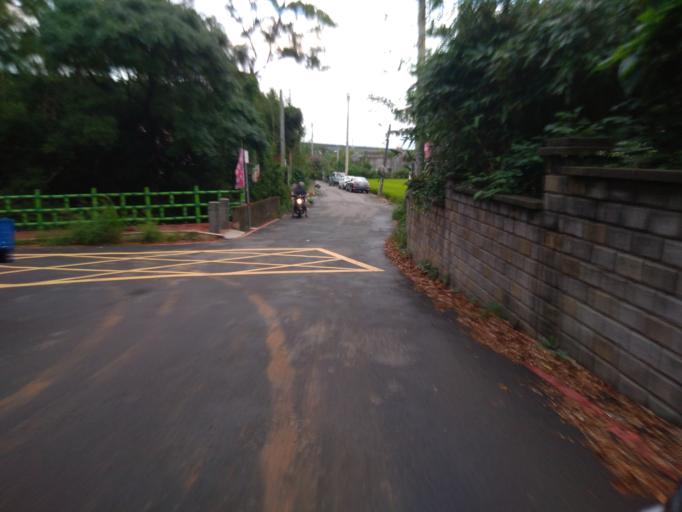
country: TW
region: Taiwan
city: Taoyuan City
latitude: 24.9457
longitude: 121.1970
